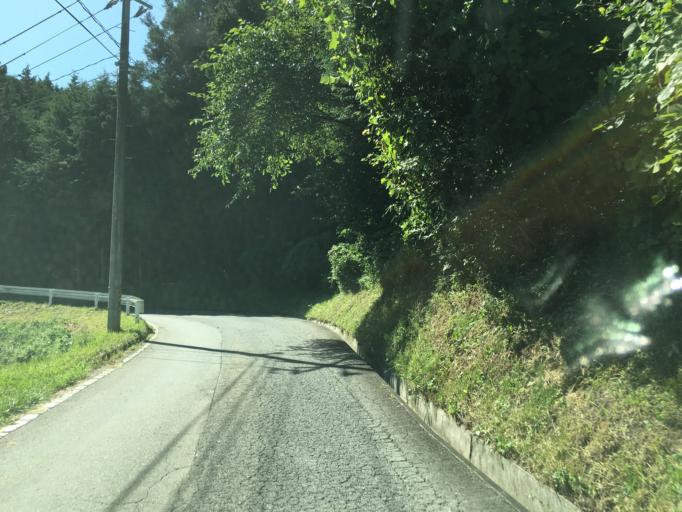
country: JP
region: Fukushima
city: Ishikawa
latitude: 37.2061
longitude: 140.5767
